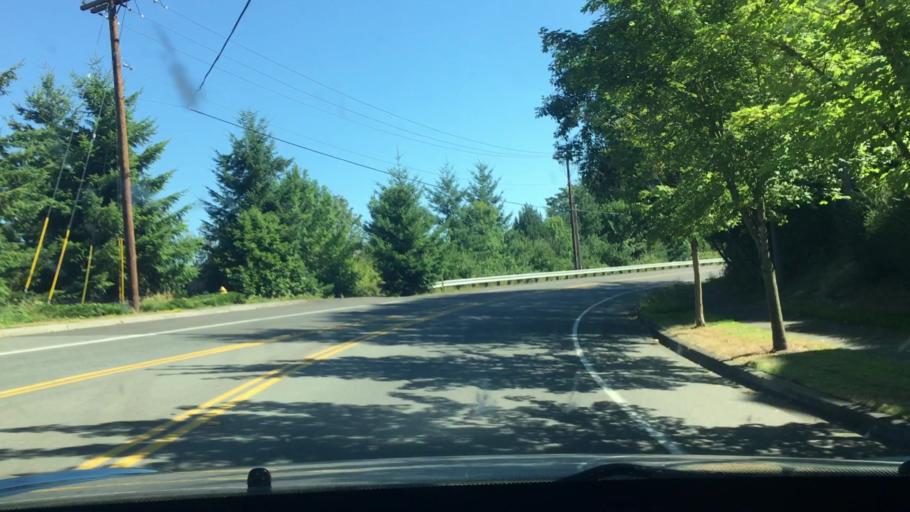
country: US
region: Washington
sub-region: King County
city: Newcastle
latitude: 47.5408
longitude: -122.1614
